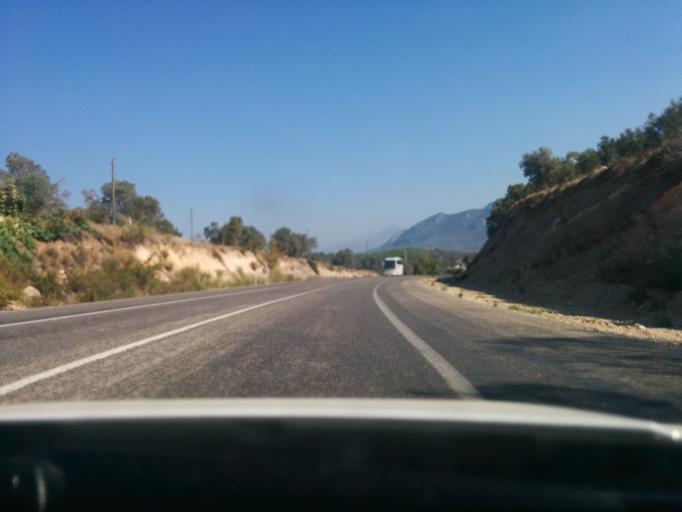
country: TR
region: Mugla
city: Esen
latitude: 36.3844
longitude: 29.3227
